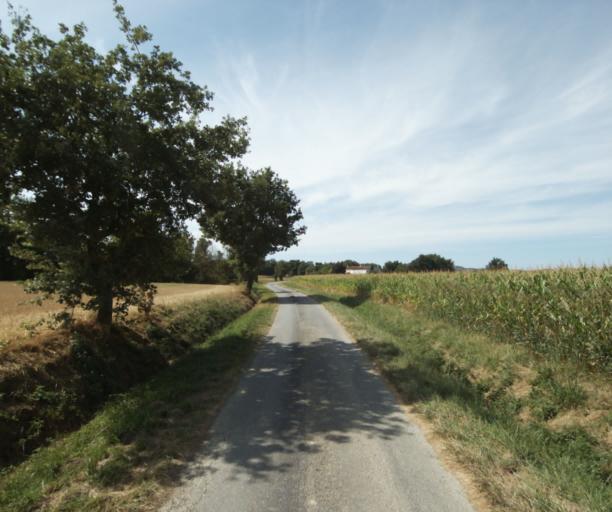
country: FR
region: Midi-Pyrenees
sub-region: Departement du Tarn
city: Soreze
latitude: 43.5130
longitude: 2.0685
